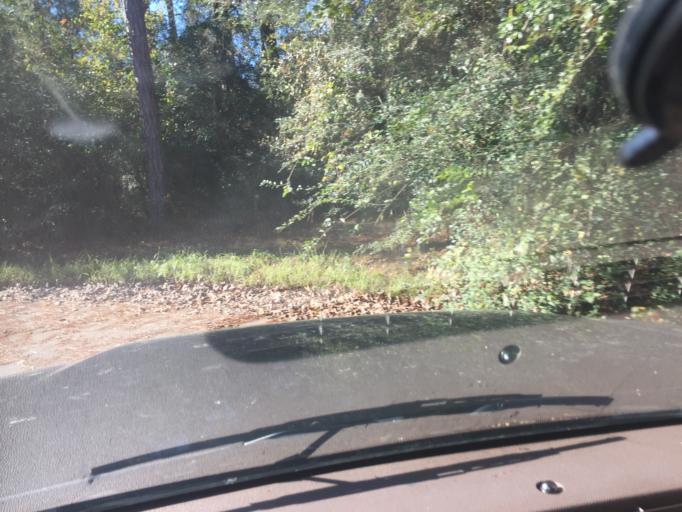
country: US
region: Louisiana
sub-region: Saint Tammany Parish
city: Slidell
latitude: 30.3095
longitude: -89.7461
